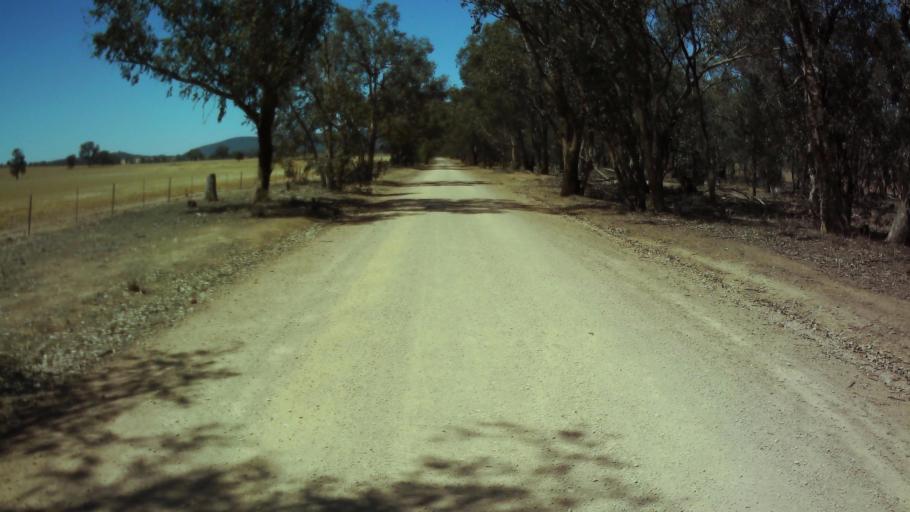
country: AU
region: New South Wales
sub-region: Weddin
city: Grenfell
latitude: -33.9132
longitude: 148.0796
